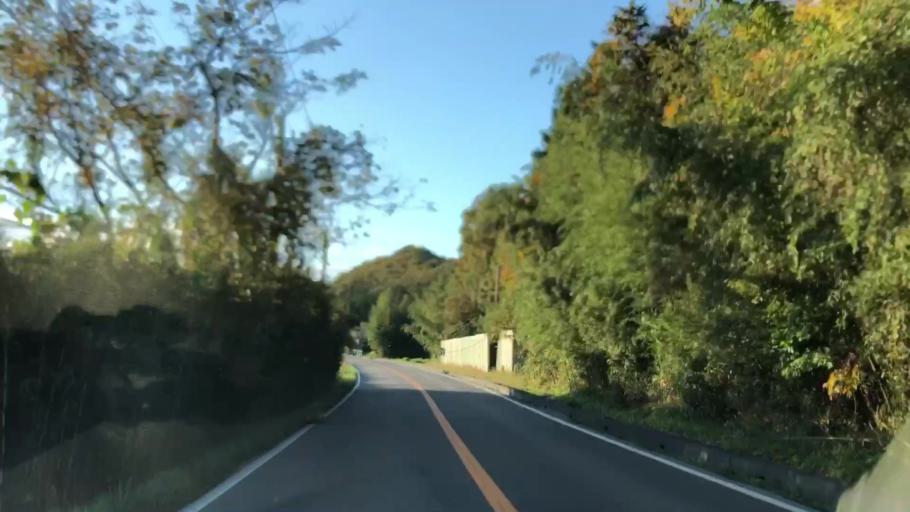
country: JP
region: Ibaraki
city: Kasama
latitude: 36.4762
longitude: 140.3039
